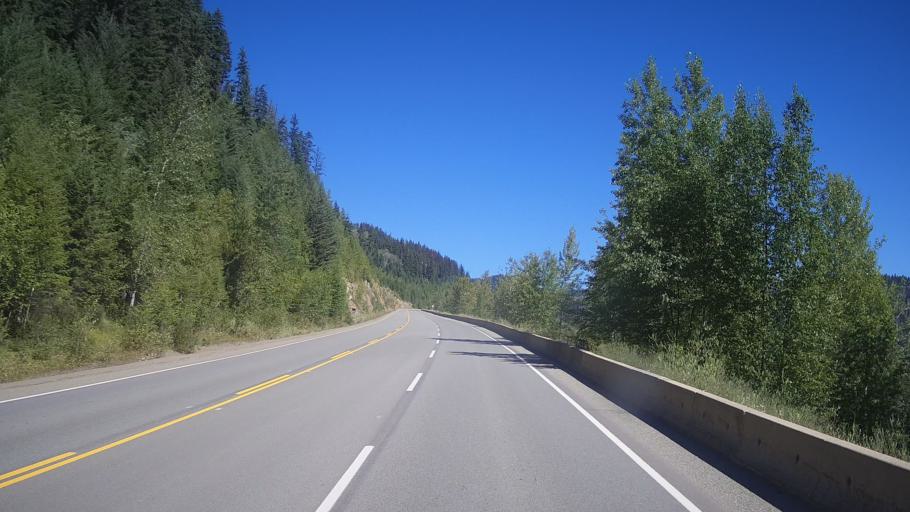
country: CA
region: British Columbia
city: Kamloops
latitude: 51.4811
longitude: -120.2609
